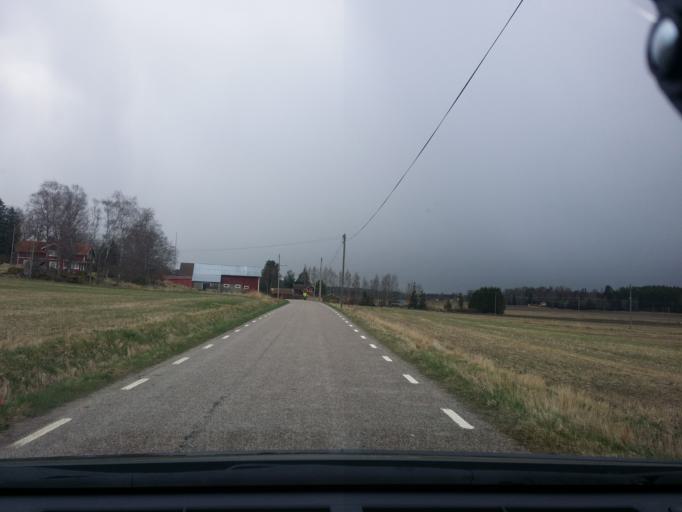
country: SE
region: Uppsala
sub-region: Enkopings Kommun
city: Enkoping
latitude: 59.6724
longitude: 17.0250
